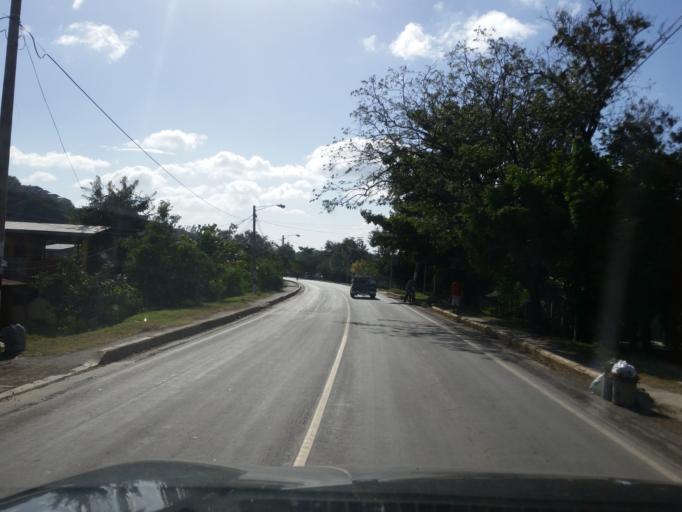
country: NI
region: Rivas
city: San Juan del Sur
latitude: 11.2622
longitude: -85.8590
